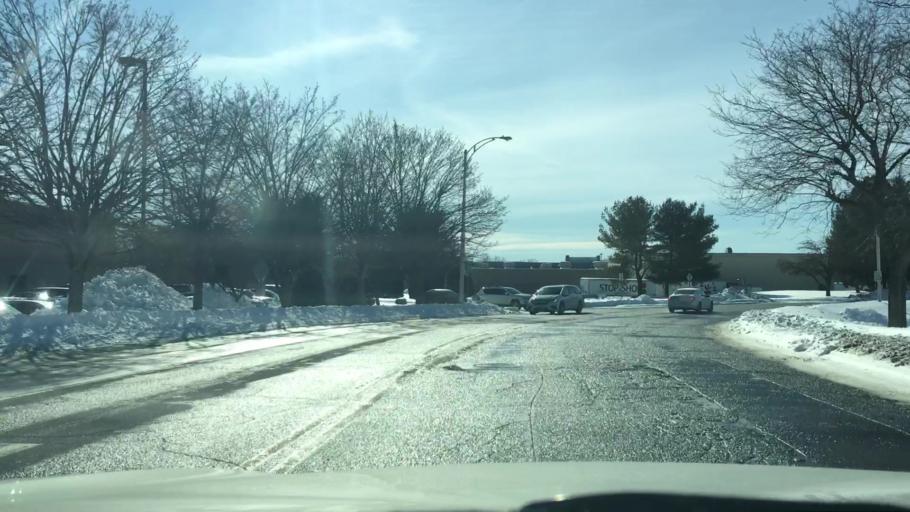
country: US
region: Massachusetts
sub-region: Hampden County
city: Chicopee
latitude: 42.1323
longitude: -72.6217
